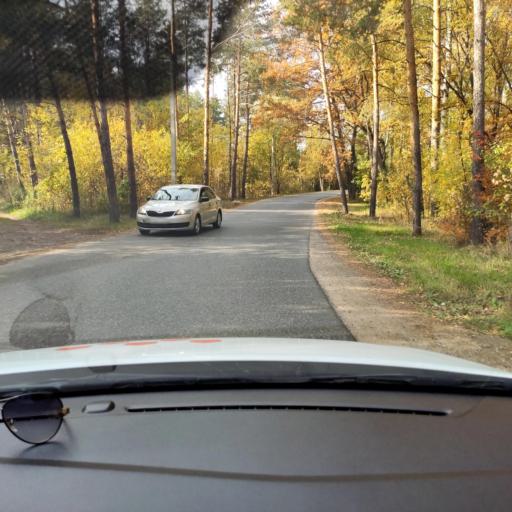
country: RU
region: Tatarstan
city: Stolbishchi
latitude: 55.6767
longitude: 49.1245
